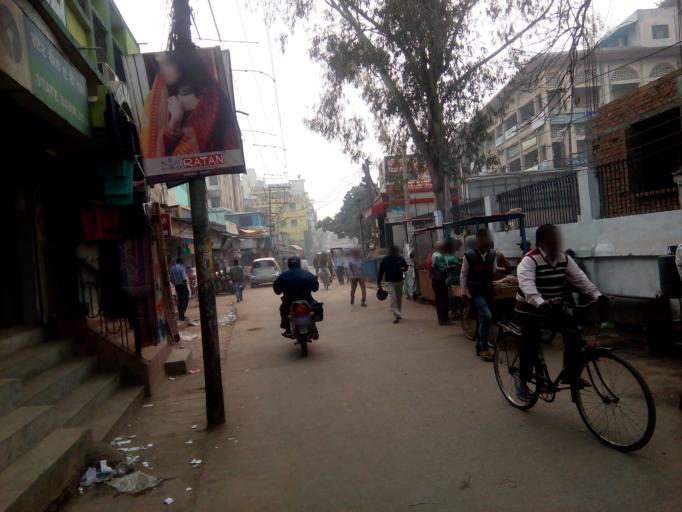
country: IN
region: Bihar
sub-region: Patna
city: Patna
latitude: 25.6167
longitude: 85.1544
